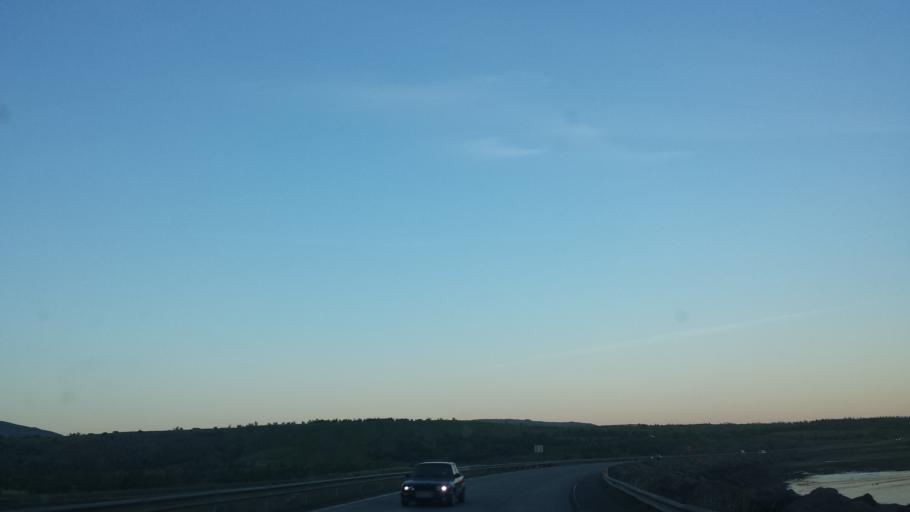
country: IS
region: Capital Region
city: Mosfellsbaer
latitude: 64.2066
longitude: -21.7102
